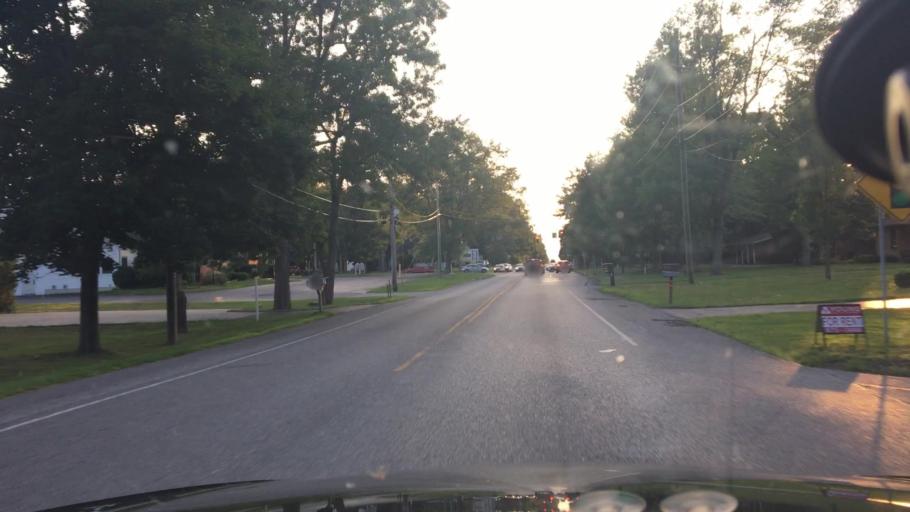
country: US
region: New York
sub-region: Erie County
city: Orchard Park
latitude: 42.7890
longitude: -78.7491
